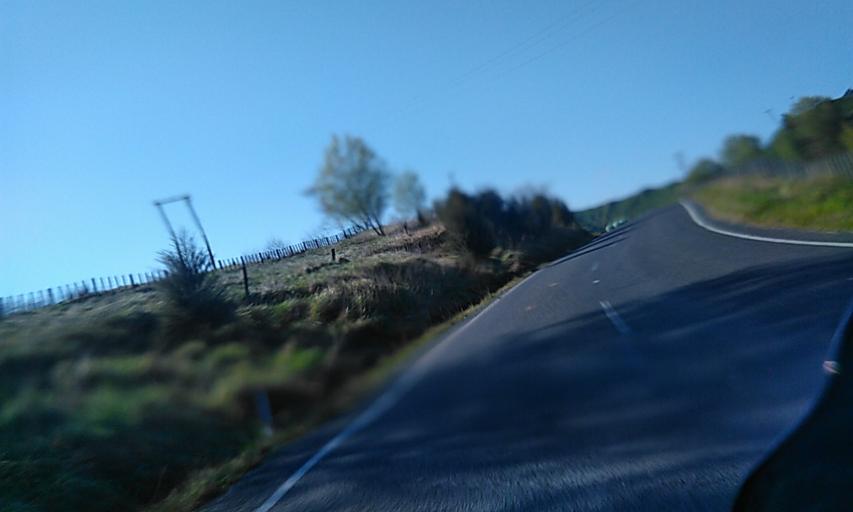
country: NZ
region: Gisborne
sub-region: Gisborne District
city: Gisborne
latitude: -38.5051
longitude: 178.0502
